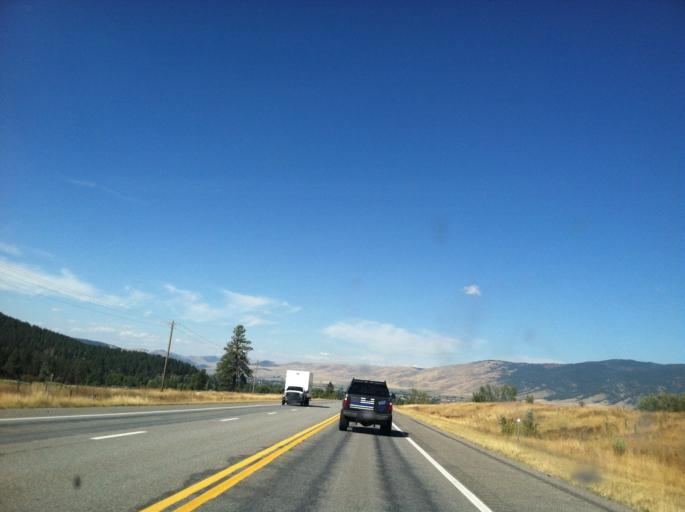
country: US
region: Montana
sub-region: Missoula County
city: Frenchtown
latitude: 47.1008
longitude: -114.0433
